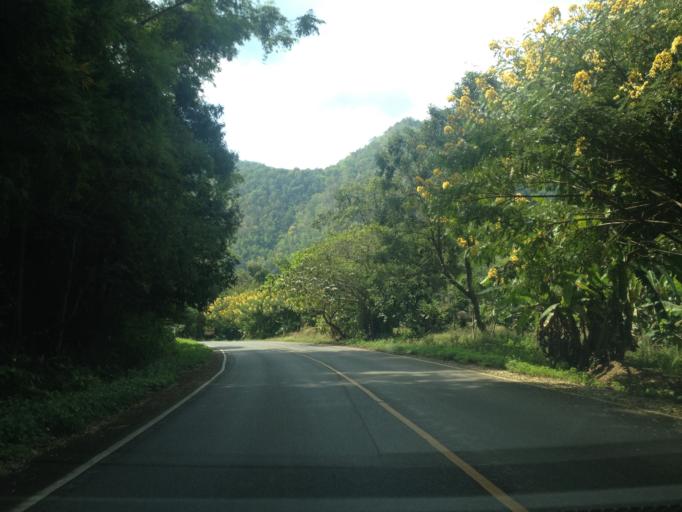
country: TH
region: Chiang Mai
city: Samoeng
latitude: 18.8041
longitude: 98.7986
